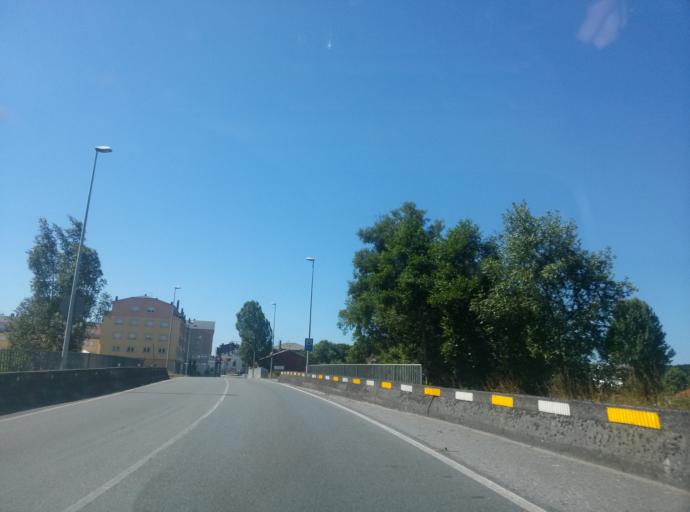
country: ES
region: Galicia
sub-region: Provincia de Lugo
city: Mos
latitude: 43.1360
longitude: -7.4900
